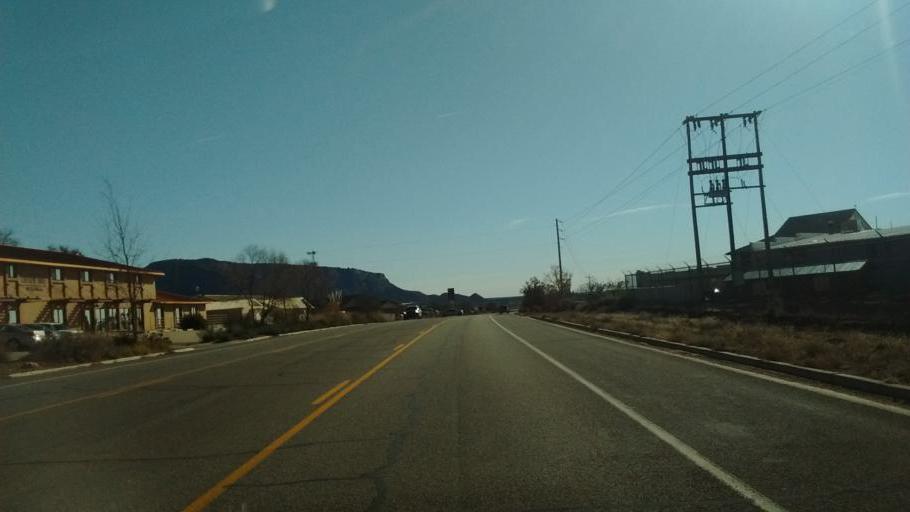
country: US
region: Arizona
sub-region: Mohave County
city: Colorado City
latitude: 37.0032
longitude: -113.0018
